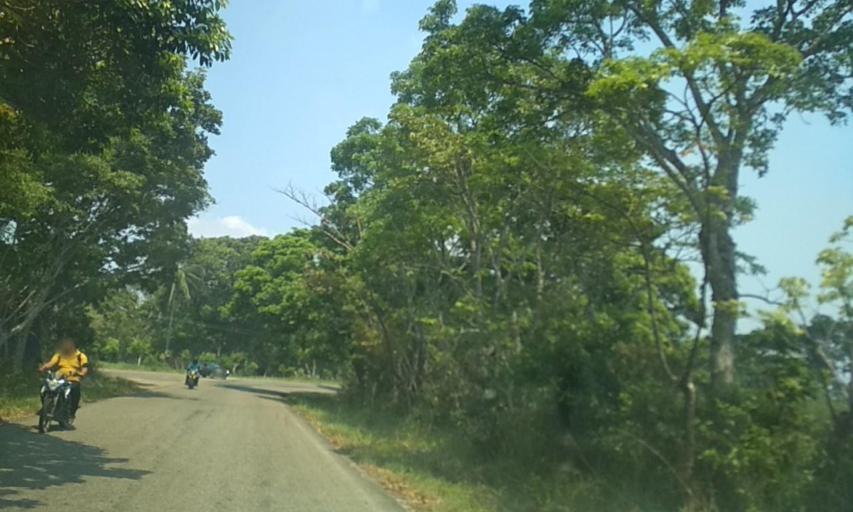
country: MX
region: Tabasco
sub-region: Huimanguillo
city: C-41 (Licenciado Carlos A. Madrazo)
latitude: 17.8497
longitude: -93.5297
